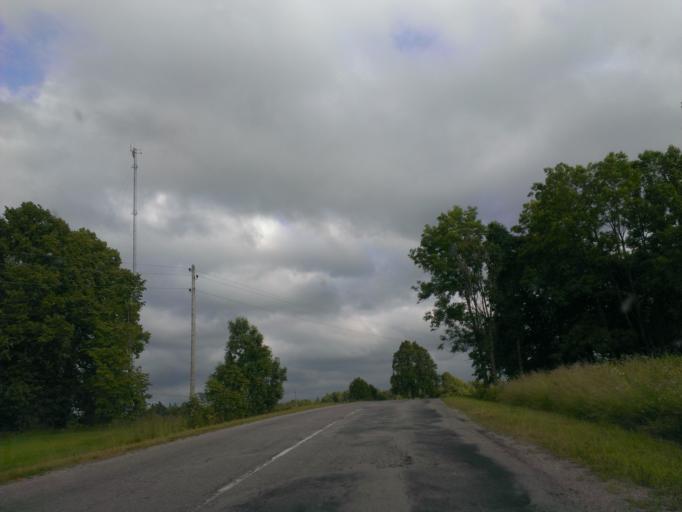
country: LV
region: Aizpute
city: Aizpute
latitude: 56.7205
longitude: 21.7575
